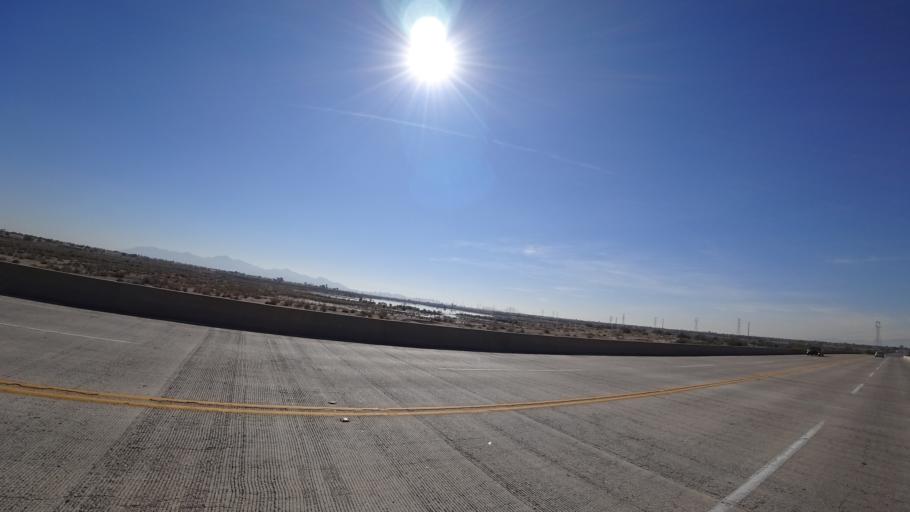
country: US
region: Arizona
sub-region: Maricopa County
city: Litchfield Park
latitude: 33.5076
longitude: -112.3076
